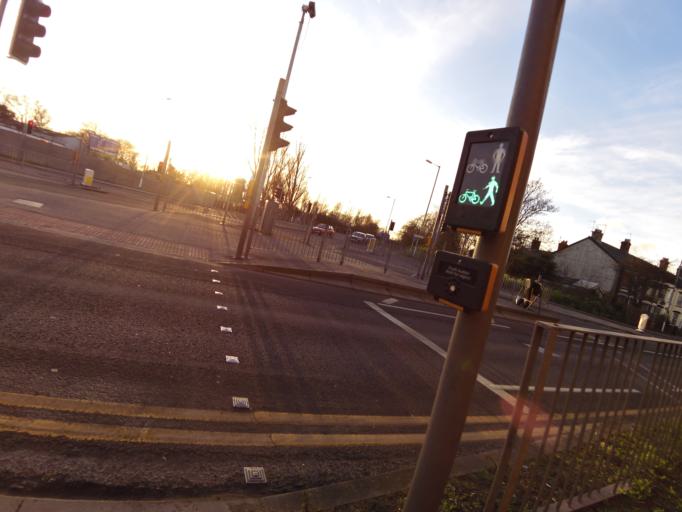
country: GB
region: England
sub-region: Norfolk
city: Great Yarmouth
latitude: 52.5911
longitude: 1.7254
